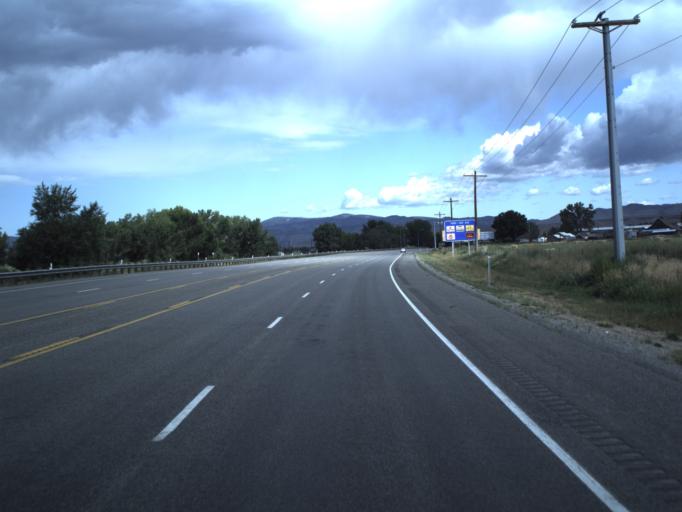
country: US
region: Utah
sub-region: Carbon County
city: Price
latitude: 39.5711
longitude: -110.7811
